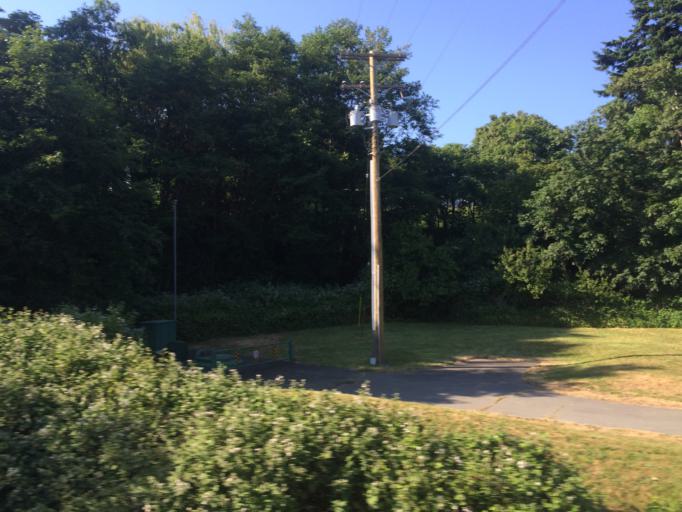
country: CA
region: British Columbia
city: Victoria
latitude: 48.4641
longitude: -123.4181
